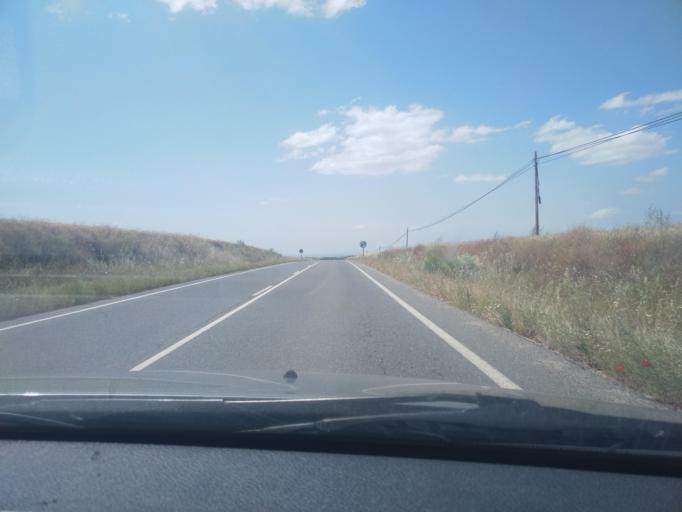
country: ES
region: Castille-La Mancha
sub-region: Province of Toledo
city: Casasbuenas
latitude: 39.7684
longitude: -4.1436
